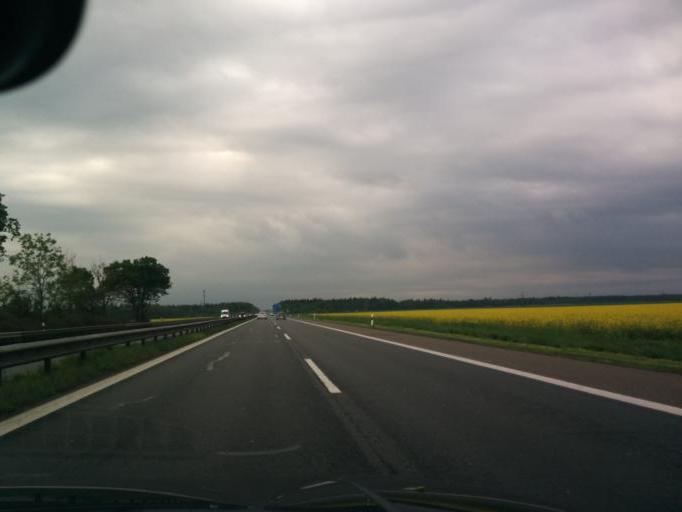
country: DE
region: Bavaria
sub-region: Upper Bavaria
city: Ottobrunn
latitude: 48.0485
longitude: 11.6469
